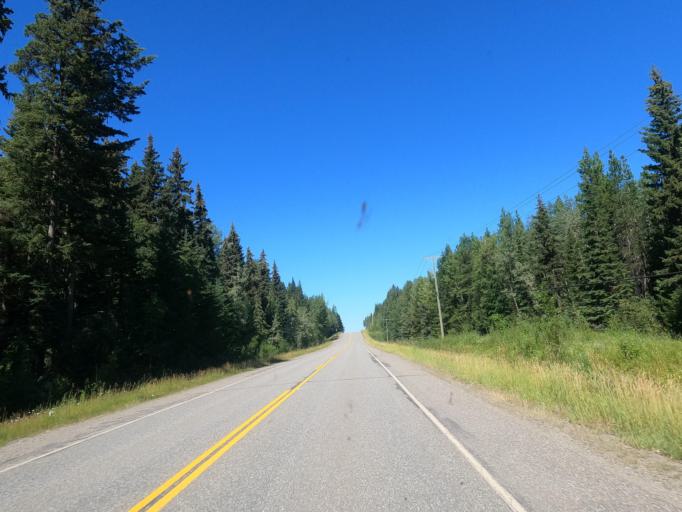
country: CA
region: British Columbia
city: Quesnel
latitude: 53.0285
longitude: -122.3893
